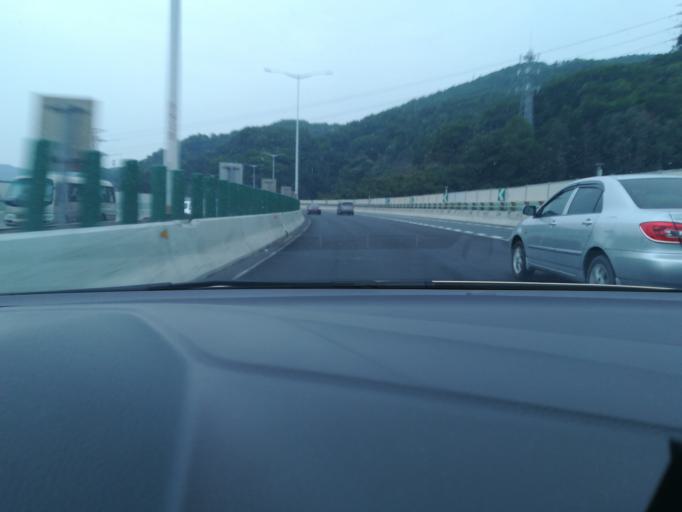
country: CN
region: Guangdong
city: Taihe
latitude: 23.2465
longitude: 113.3560
